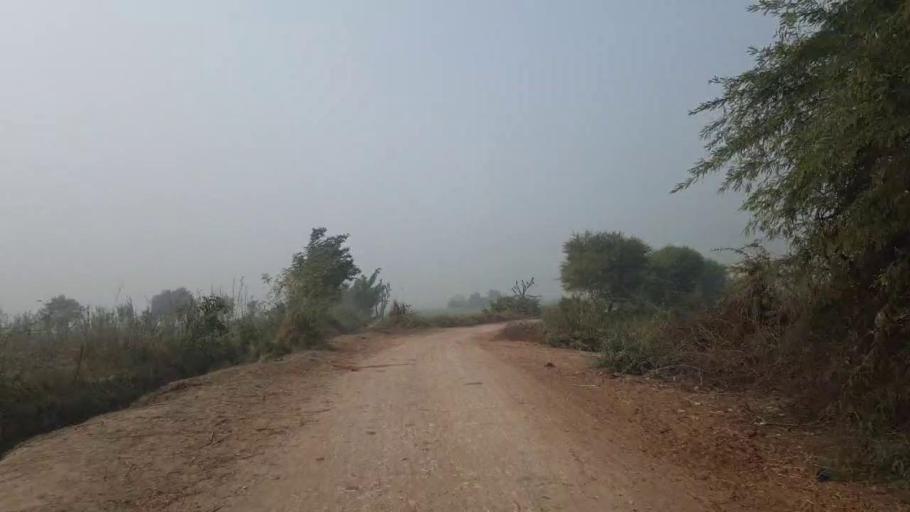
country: PK
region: Sindh
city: Bhit Shah
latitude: 25.8057
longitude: 68.5629
